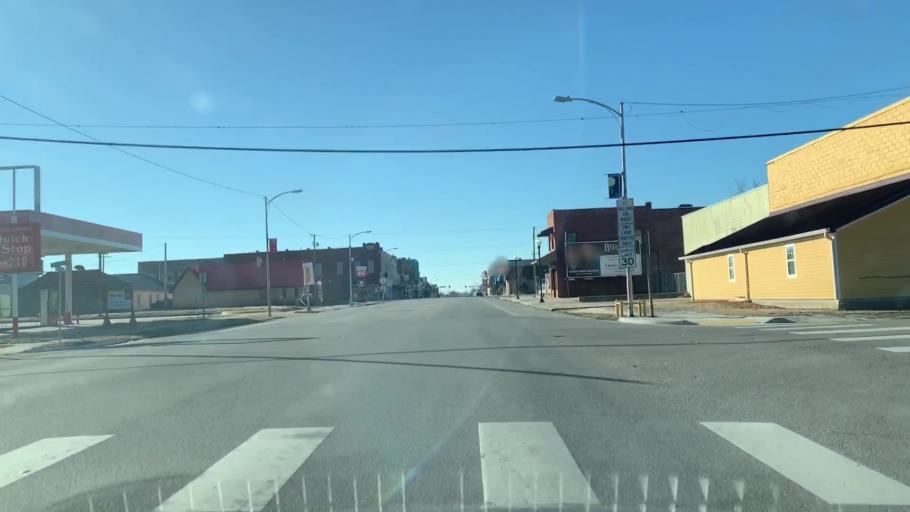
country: US
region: Kansas
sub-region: Cherokee County
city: Baxter Springs
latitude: 37.0268
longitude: -94.7352
